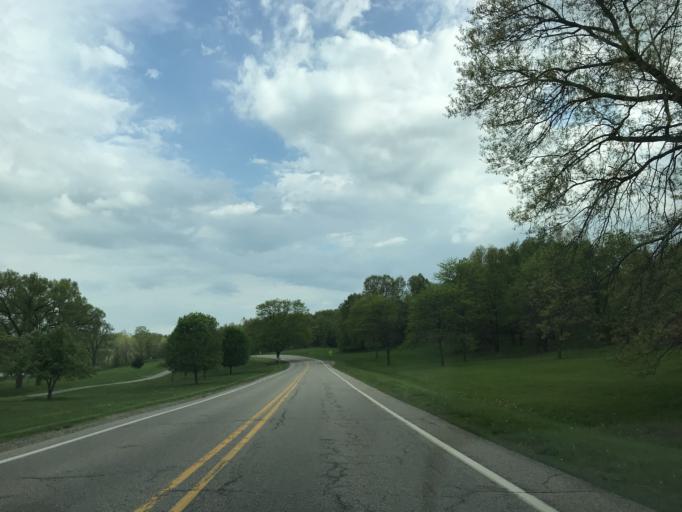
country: US
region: Michigan
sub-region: Oakland County
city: Milford
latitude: 42.5469
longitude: -83.6403
